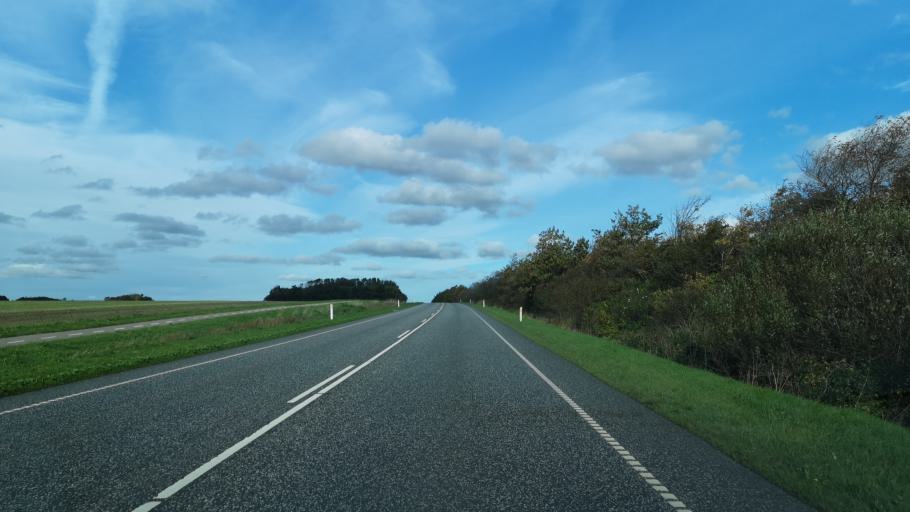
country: DK
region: Central Jutland
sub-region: Holstebro Kommune
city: Holstebro
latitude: 56.3215
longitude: 8.6089
